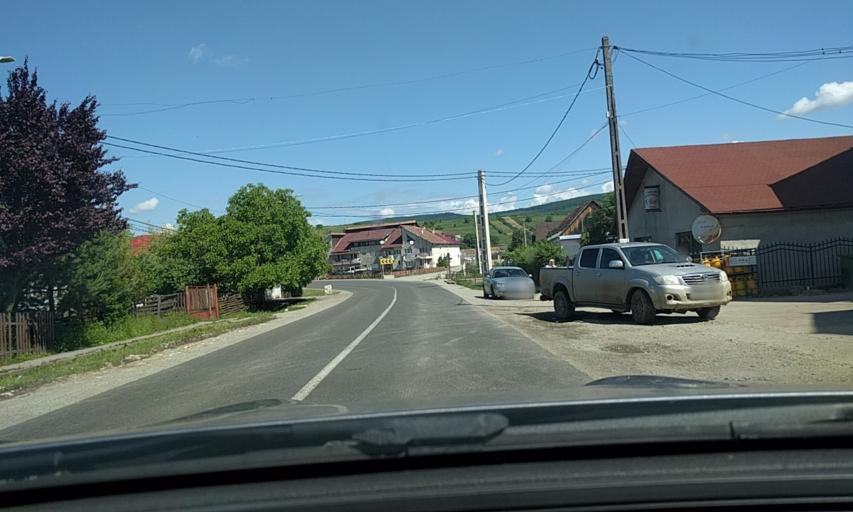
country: RO
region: Bistrita-Nasaud
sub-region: Comuna Dumitra
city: Dumitra
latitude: 47.2220
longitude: 24.4681
